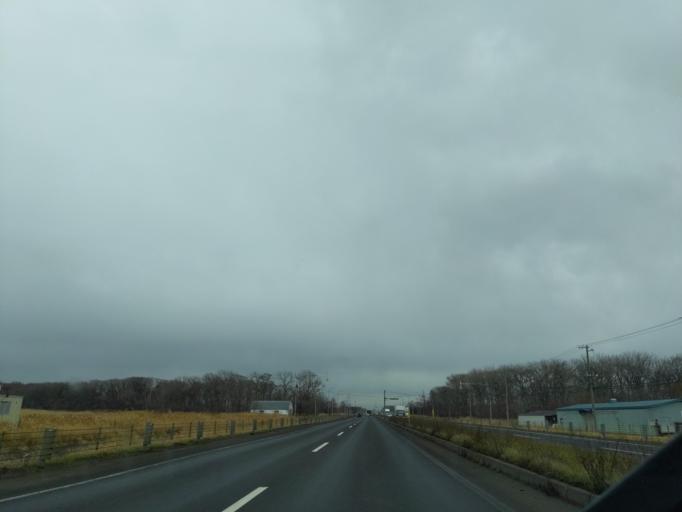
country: JP
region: Hokkaido
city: Ishikari
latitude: 43.1807
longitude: 141.3544
